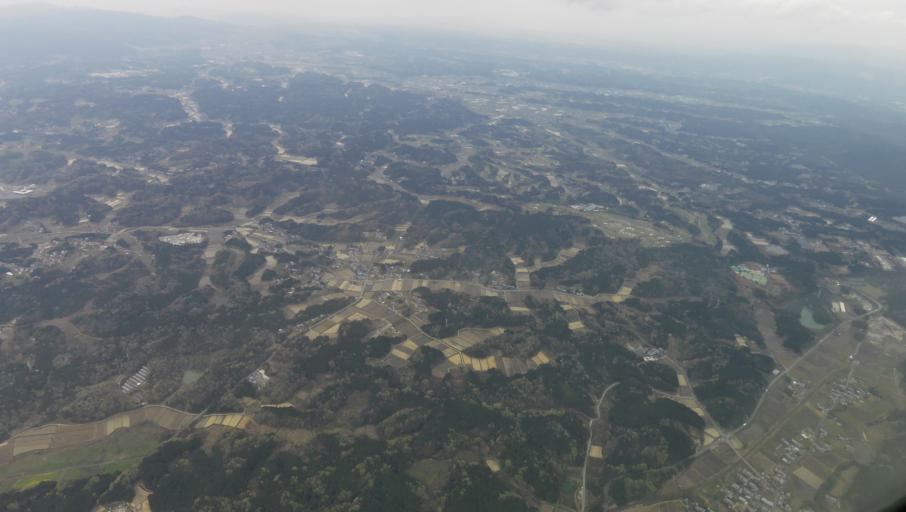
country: JP
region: Mie
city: Ueno-ebisumachi
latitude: 34.8373
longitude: 136.2345
